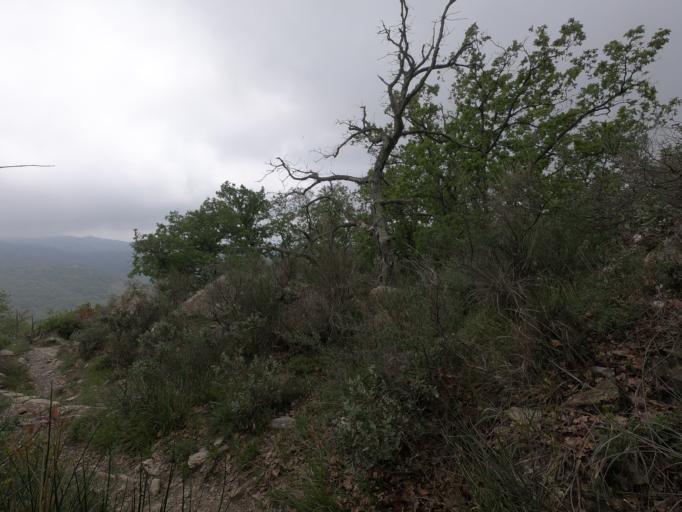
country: IT
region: Liguria
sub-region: Provincia di Imperia
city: Villa Faraldi
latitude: 43.9705
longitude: 8.0896
